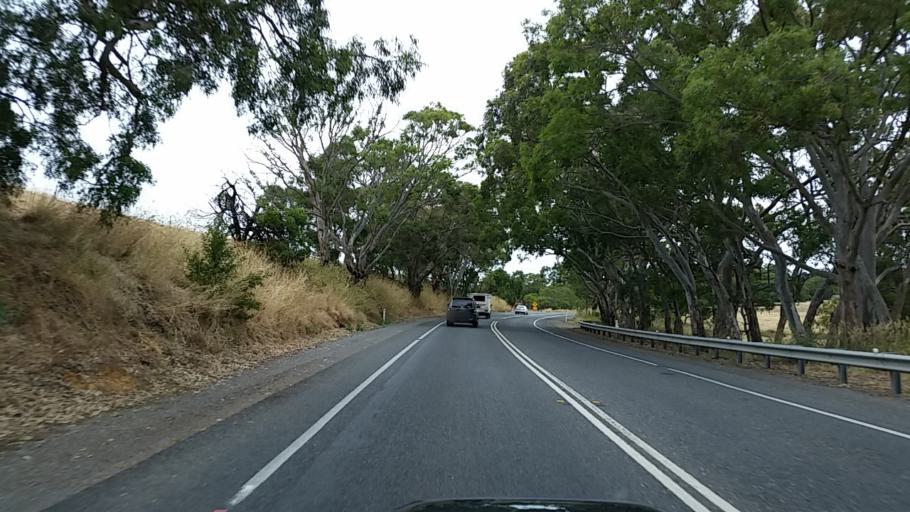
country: AU
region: South Australia
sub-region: Onkaparinga
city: Aldinga
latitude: -35.3665
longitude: 138.4569
